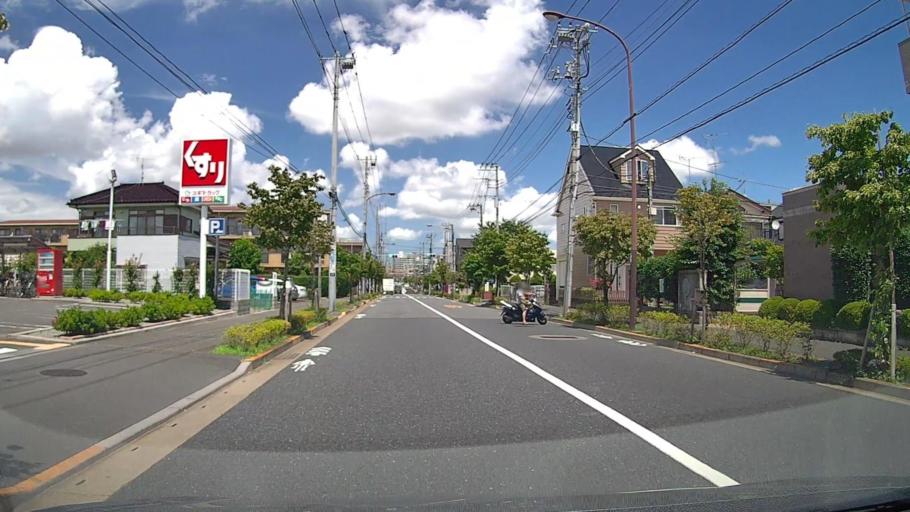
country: JP
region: Tokyo
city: Nishi-Tokyo-shi
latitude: 35.7338
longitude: 139.5432
